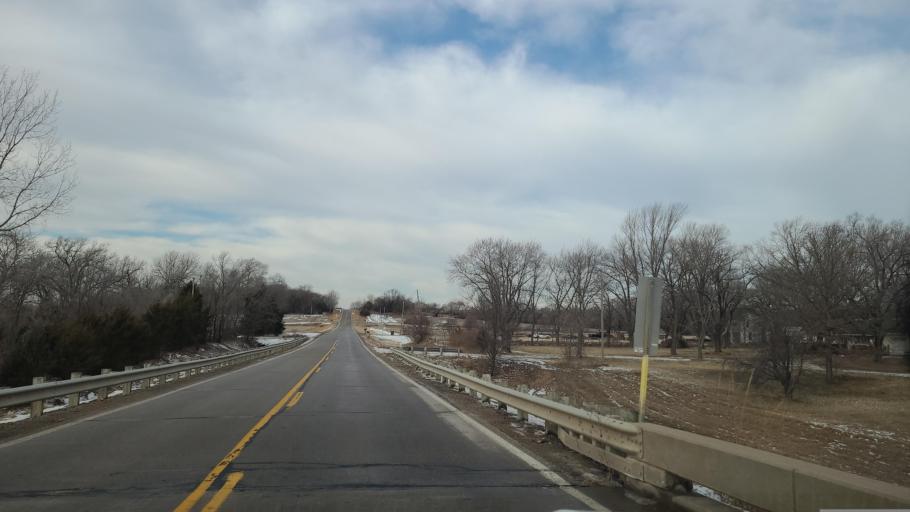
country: US
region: Kansas
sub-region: Douglas County
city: Lawrence
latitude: 39.0438
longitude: -95.4049
